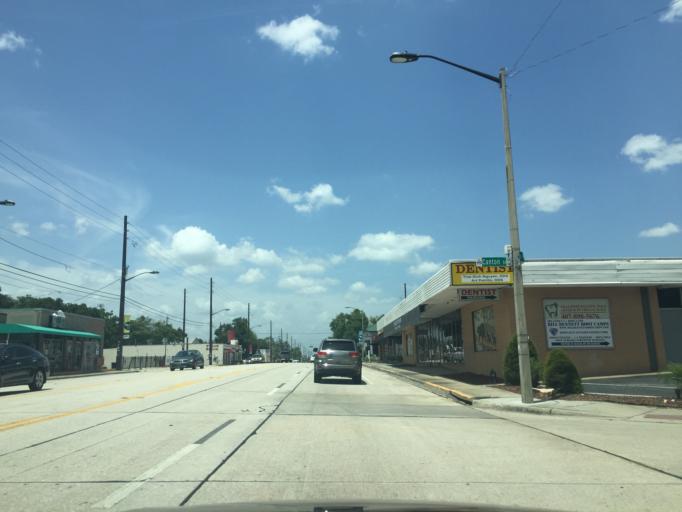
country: US
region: Florida
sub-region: Orange County
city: Orlando
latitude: 28.5594
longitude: -81.3644
